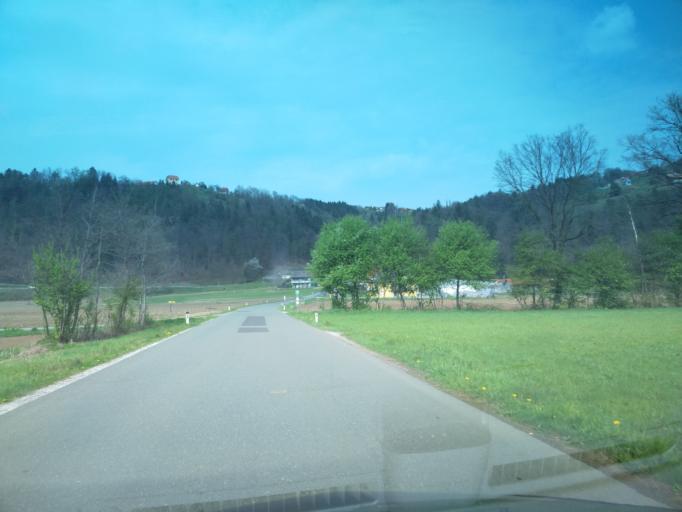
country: AT
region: Styria
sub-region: Politischer Bezirk Leibnitz
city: Kitzeck im Sausal
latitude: 46.7592
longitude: 15.4069
